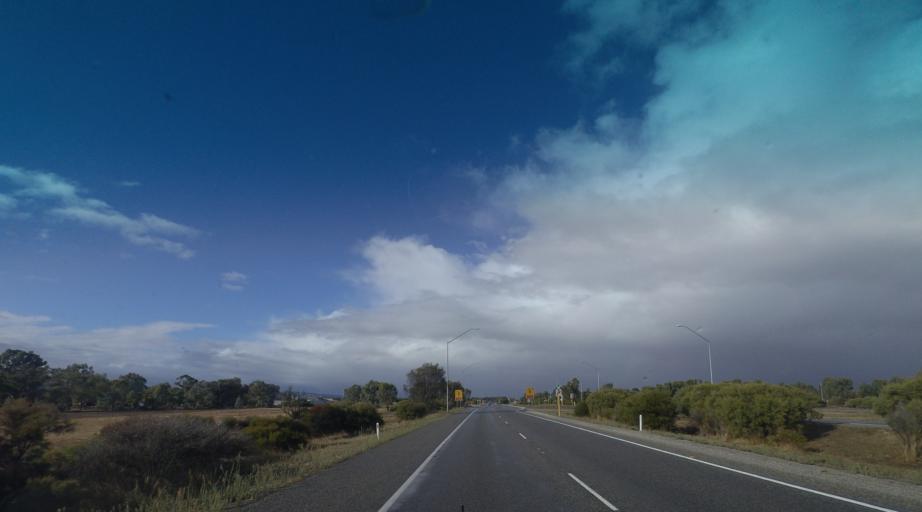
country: AU
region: Western Australia
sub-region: Serpentine-Jarrahdale
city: Oakford
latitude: -32.1777
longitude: 115.9619
